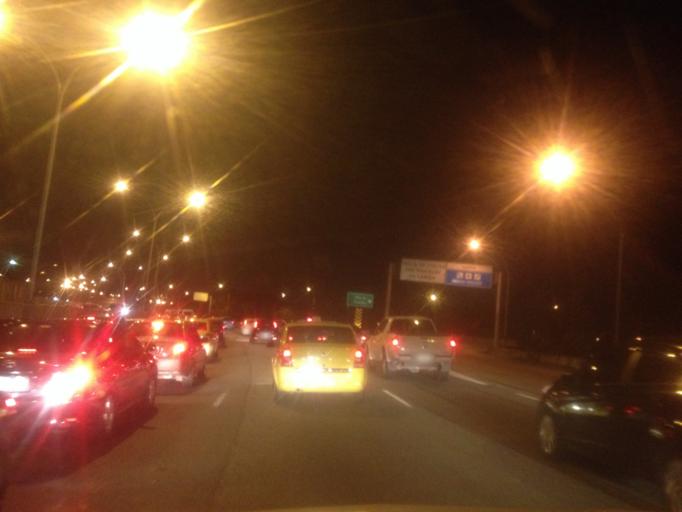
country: BR
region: Rio de Janeiro
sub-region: Rio De Janeiro
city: Rio de Janeiro
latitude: -22.8648
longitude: -43.2336
